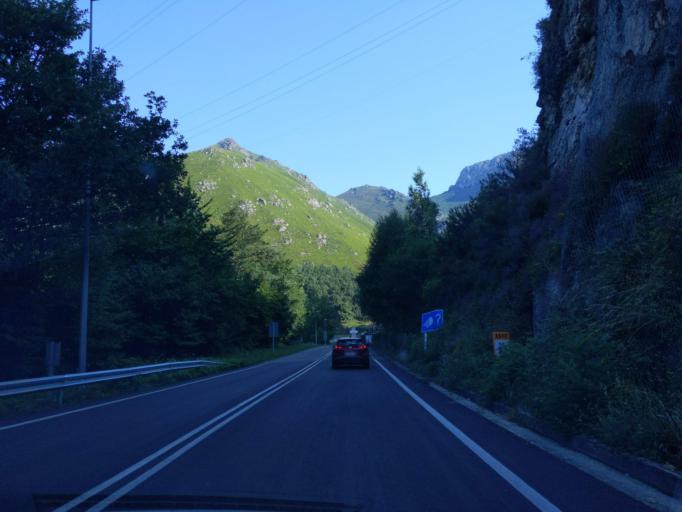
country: ES
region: Asturias
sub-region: Province of Asturias
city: Pola de Laviana
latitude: 43.2303
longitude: -5.4739
